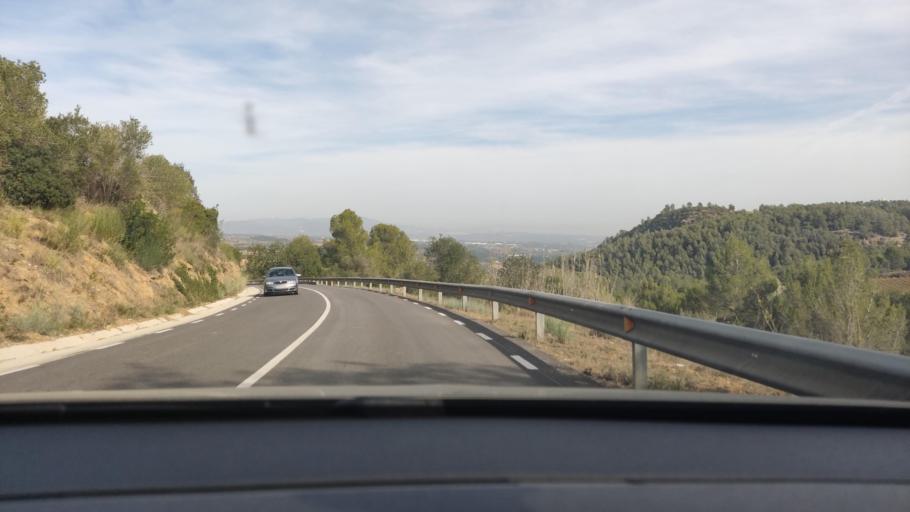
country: ES
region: Catalonia
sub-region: Provincia de Barcelona
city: Sant Sadurni d'Anoia
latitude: 41.4130
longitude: 1.8020
